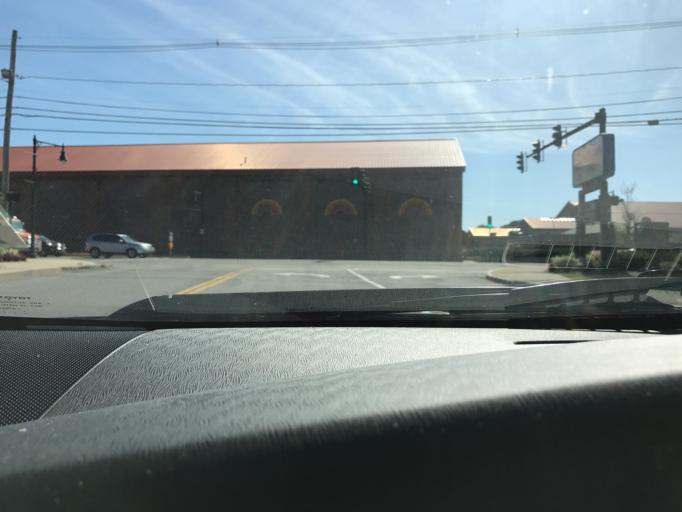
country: US
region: Massachusetts
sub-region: Middlesex County
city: Watertown
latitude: 42.3633
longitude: -71.1575
